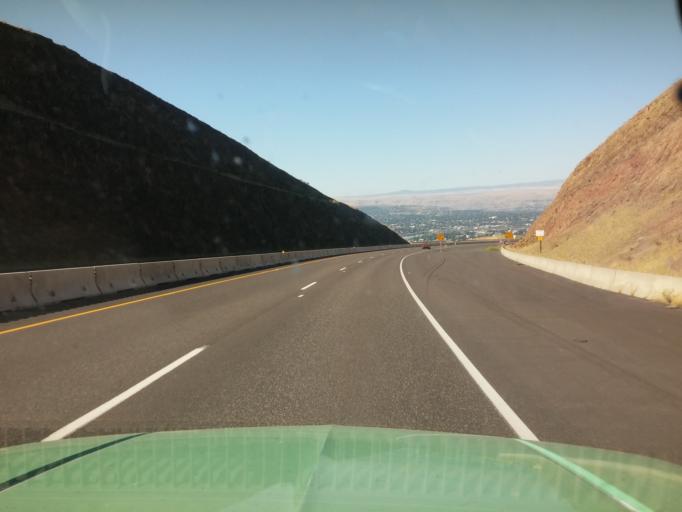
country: US
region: Idaho
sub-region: Nez Perce County
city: Lewiston
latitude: 46.4497
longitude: -116.9715
